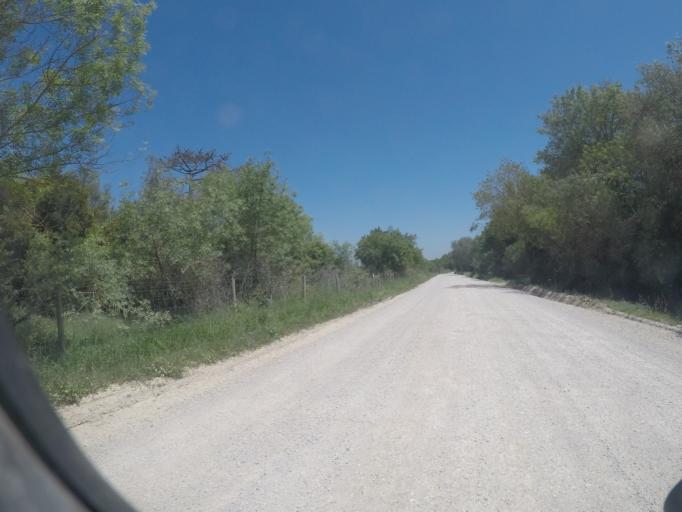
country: PT
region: Setubal
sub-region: Sesimbra
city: Sesimbra
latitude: 38.4619
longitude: -9.0553
